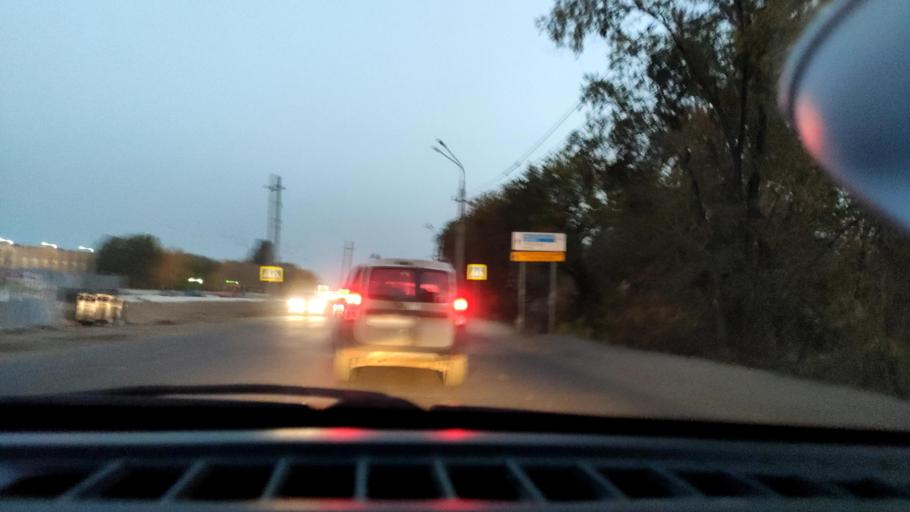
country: RU
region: Samara
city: Samara
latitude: 53.1410
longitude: 50.1000
